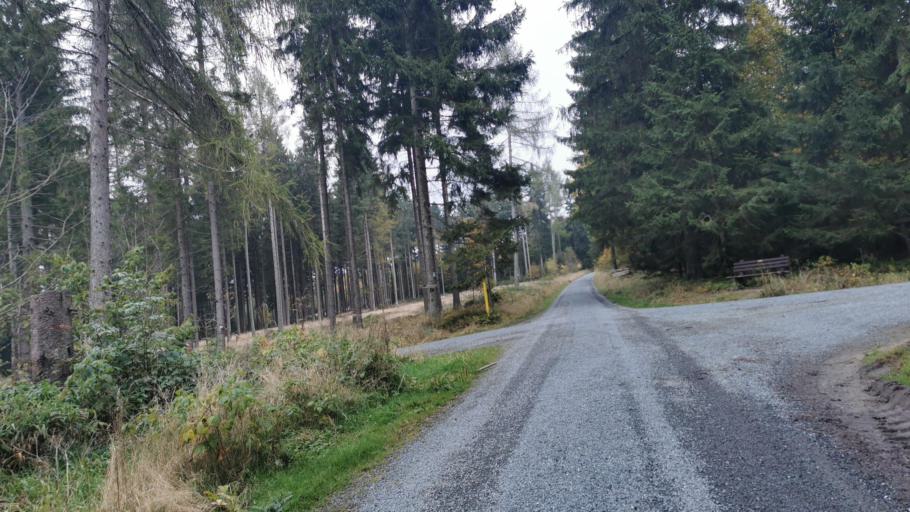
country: DE
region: Bavaria
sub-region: Upper Franconia
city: Ludwigsstadt
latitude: 50.4450
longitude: 11.3531
